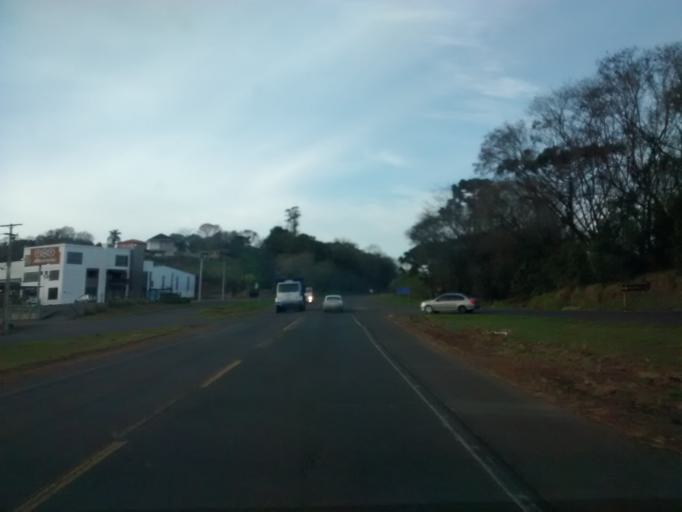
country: BR
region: Parana
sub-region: Francisco Beltrao
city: Francisco Beltrao
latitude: -26.1029
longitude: -53.0584
